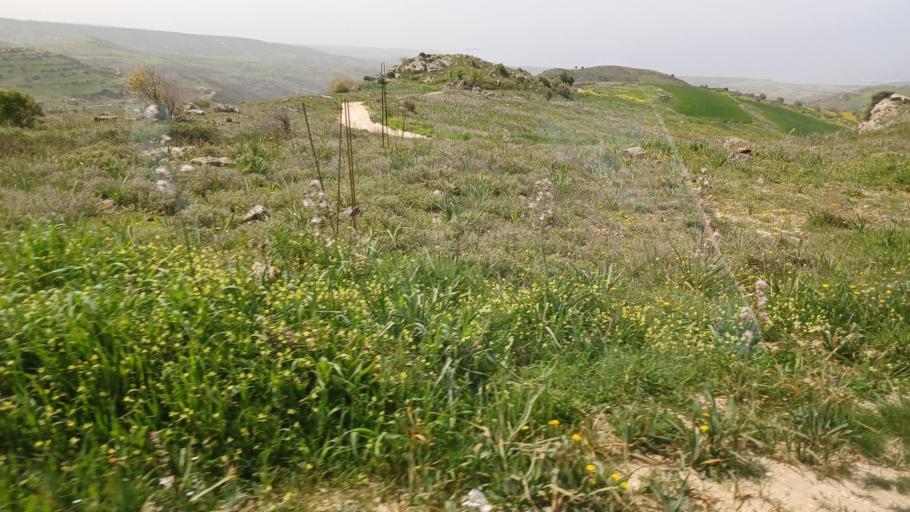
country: CY
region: Pafos
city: Polis
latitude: 34.9759
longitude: 32.3603
